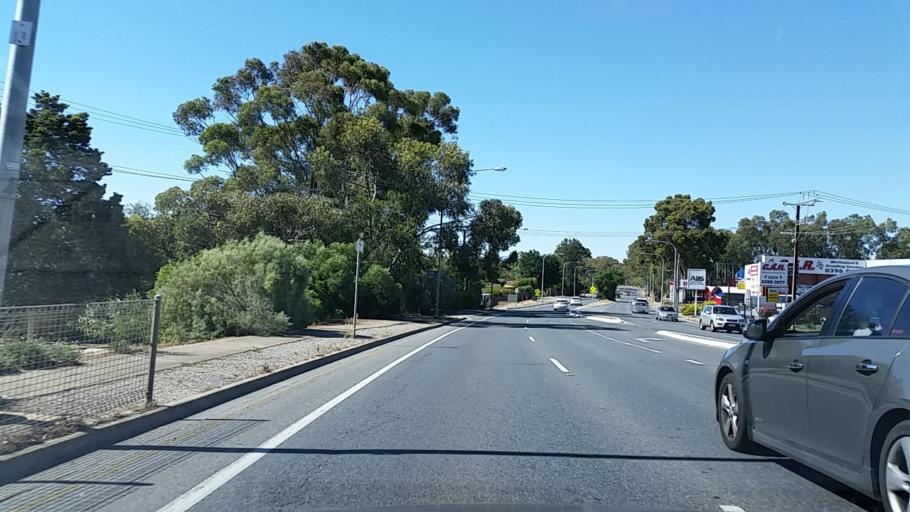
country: AU
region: South Australia
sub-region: Tea Tree Gully
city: Hope Valley
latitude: -34.8260
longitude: 138.6936
